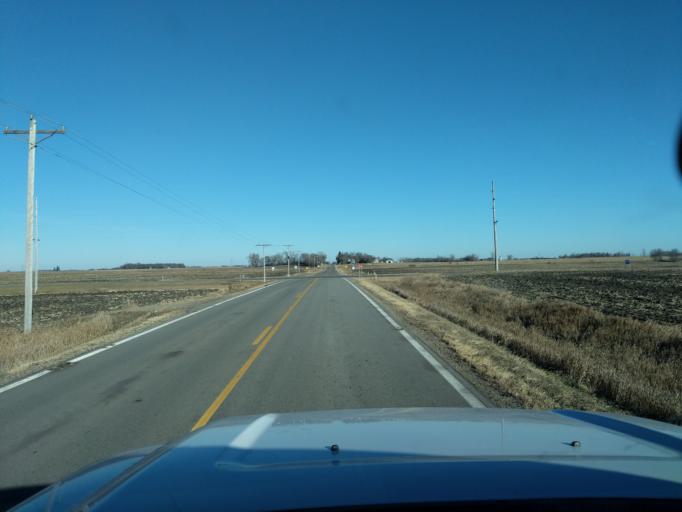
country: US
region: Minnesota
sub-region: Yellow Medicine County
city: Granite Falls
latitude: 44.7879
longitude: -95.4017
